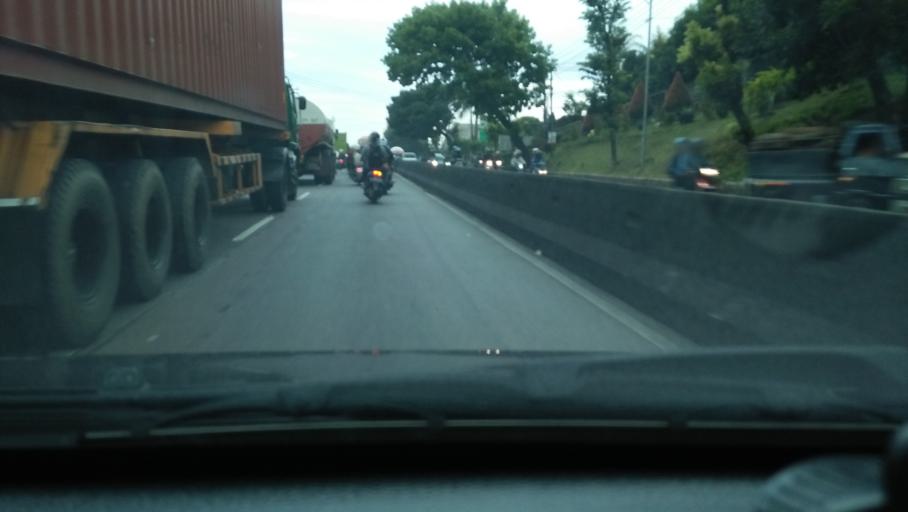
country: ID
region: Central Java
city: Ungaran
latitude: -7.1780
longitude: 110.4199
